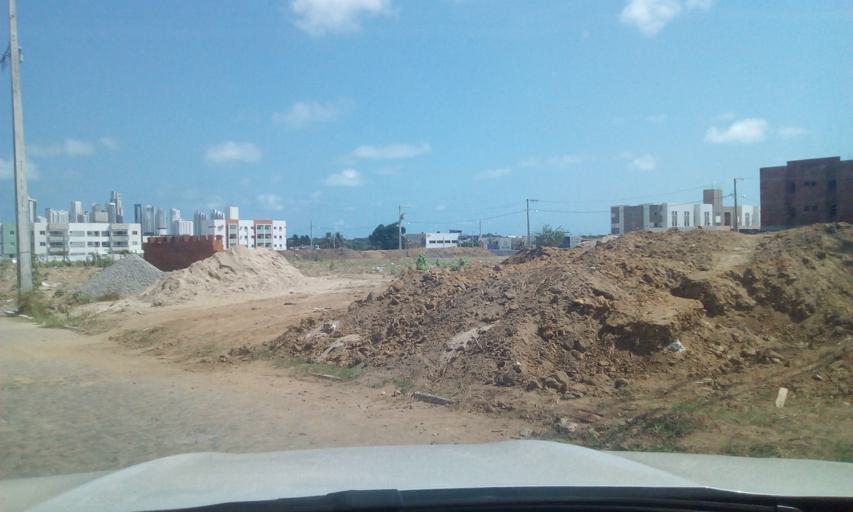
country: BR
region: Paraiba
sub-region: Joao Pessoa
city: Joao Pessoa
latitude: -7.1514
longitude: -34.8316
